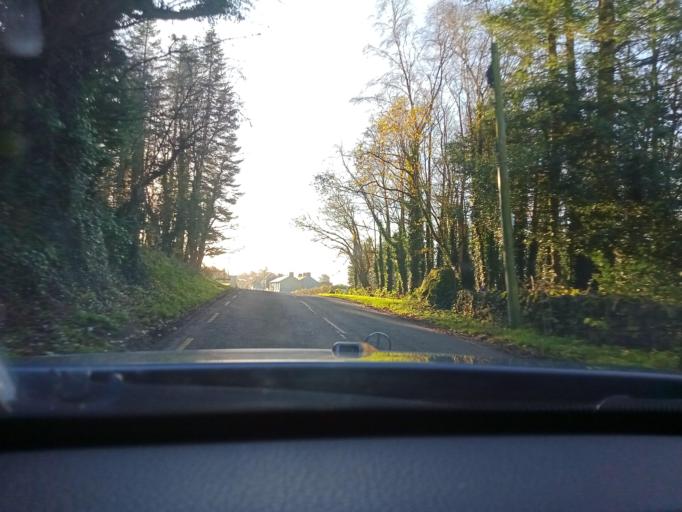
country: IE
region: Leinster
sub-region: Kilkenny
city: Callan
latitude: 52.4630
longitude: -7.3943
